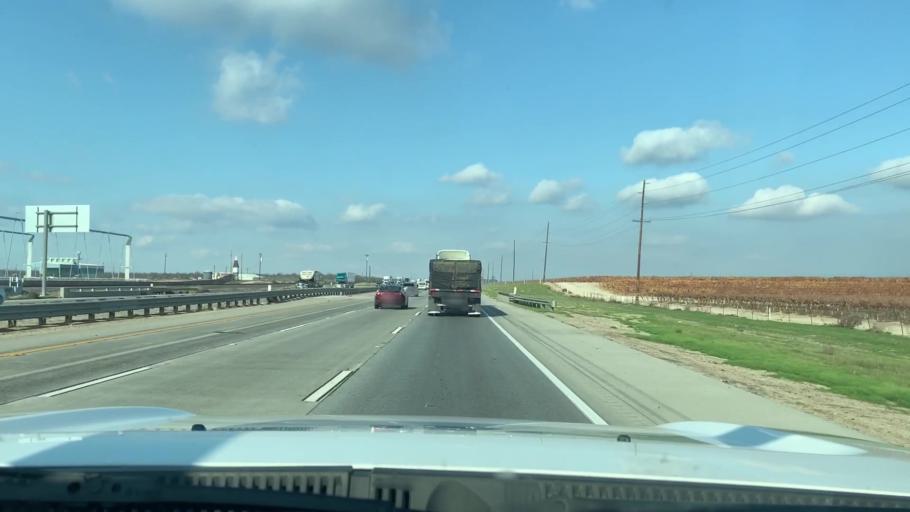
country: US
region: California
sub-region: Kern County
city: Shafter
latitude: 35.5679
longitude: -119.2002
